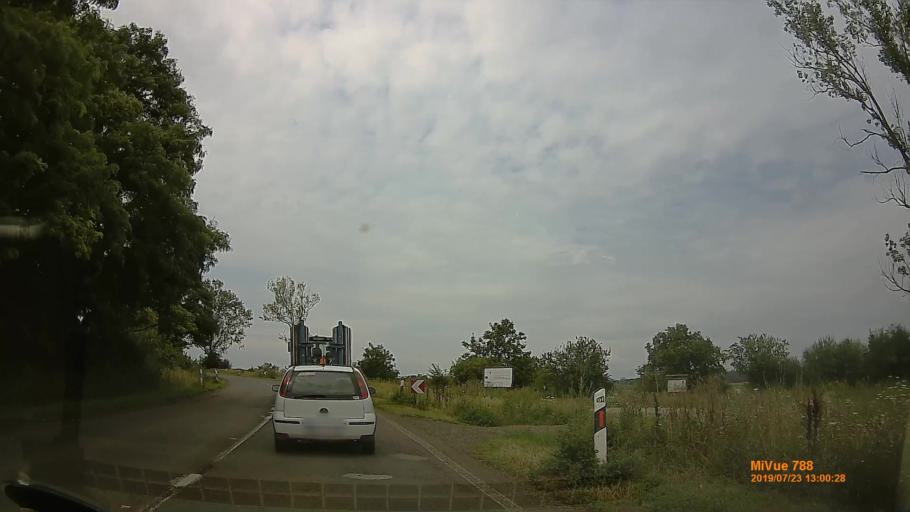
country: HU
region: Szabolcs-Szatmar-Bereg
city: Tiszalok
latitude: 47.9588
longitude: 21.4224
